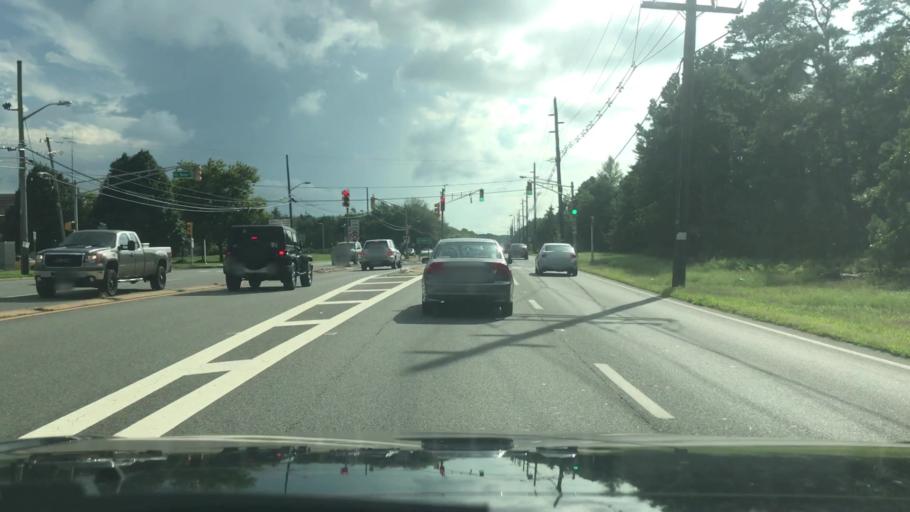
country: US
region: New Jersey
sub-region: Ocean County
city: Leisure Village East
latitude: 40.0056
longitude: -74.1504
